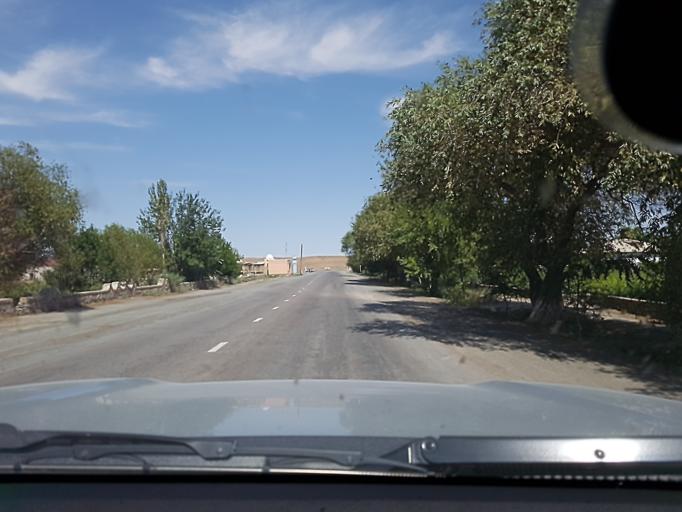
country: UZ
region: Karakalpakstan
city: Mang'it Shahri
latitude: 42.2433
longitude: 60.1503
